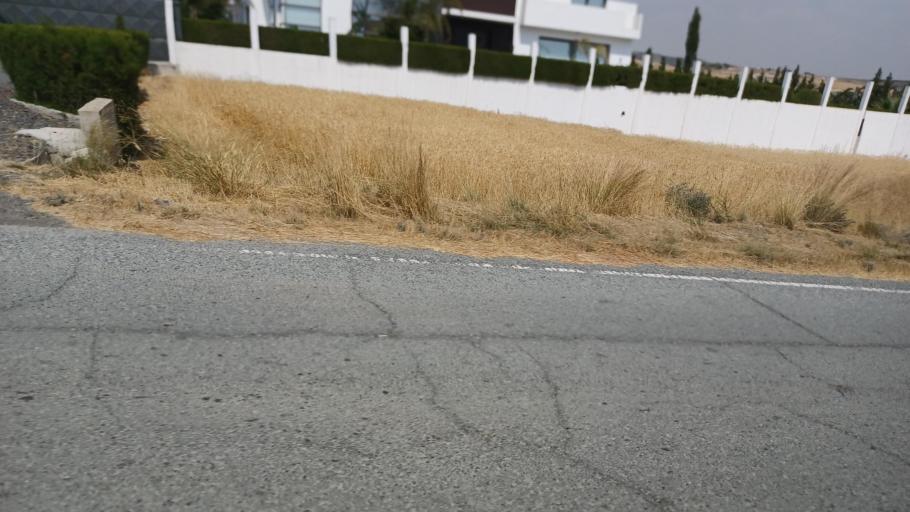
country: CY
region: Larnaka
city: Aradippou
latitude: 34.9449
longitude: 33.5609
